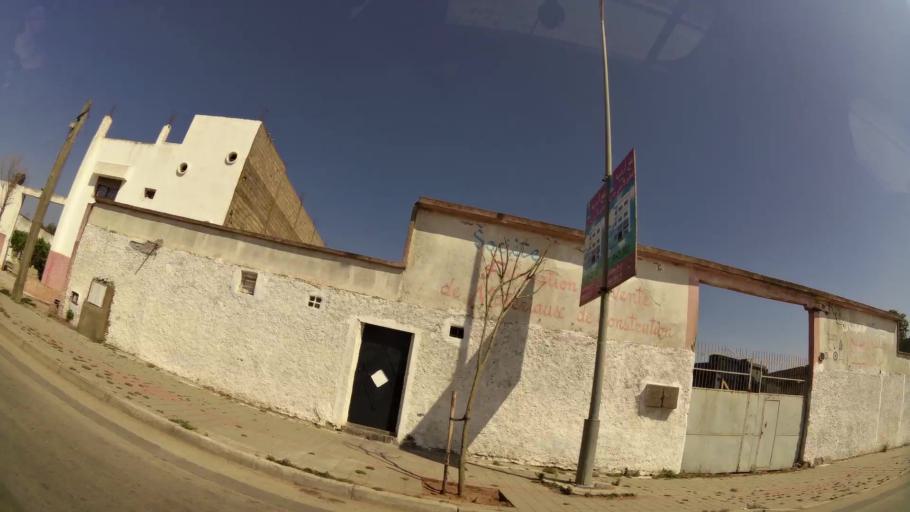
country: MA
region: Rabat-Sale-Zemmour-Zaer
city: Sale
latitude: 34.0763
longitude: -6.7539
